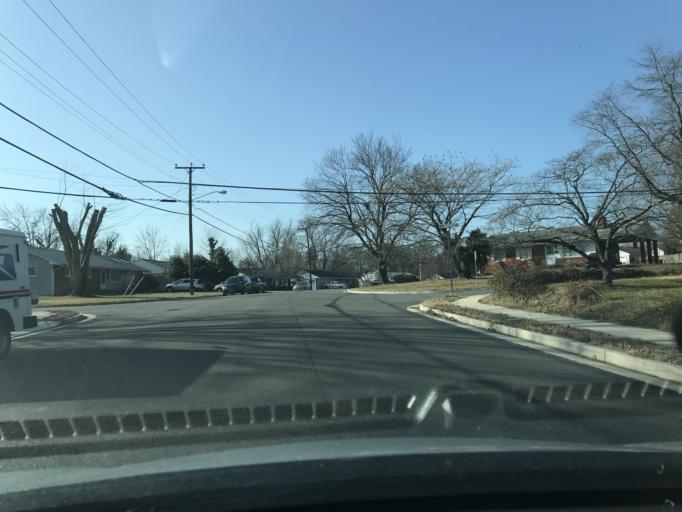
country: US
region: Virginia
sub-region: City of Fairfax
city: Fairfax
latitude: 38.8545
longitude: -77.3218
